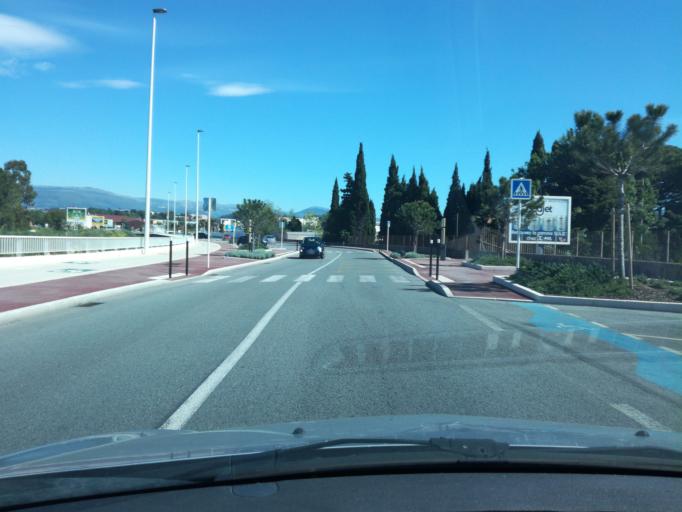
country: FR
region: Provence-Alpes-Cote d'Azur
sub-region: Departement des Alpes-Maritimes
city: Mandelieu-la-Napoule
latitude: 43.5460
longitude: 6.9622
